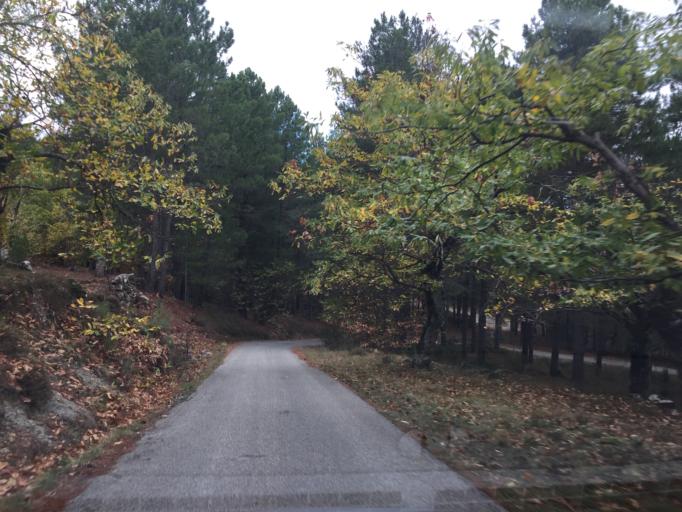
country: FR
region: Rhone-Alpes
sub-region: Departement de l'Ardeche
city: Les Vans
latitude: 44.4261
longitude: 4.0764
